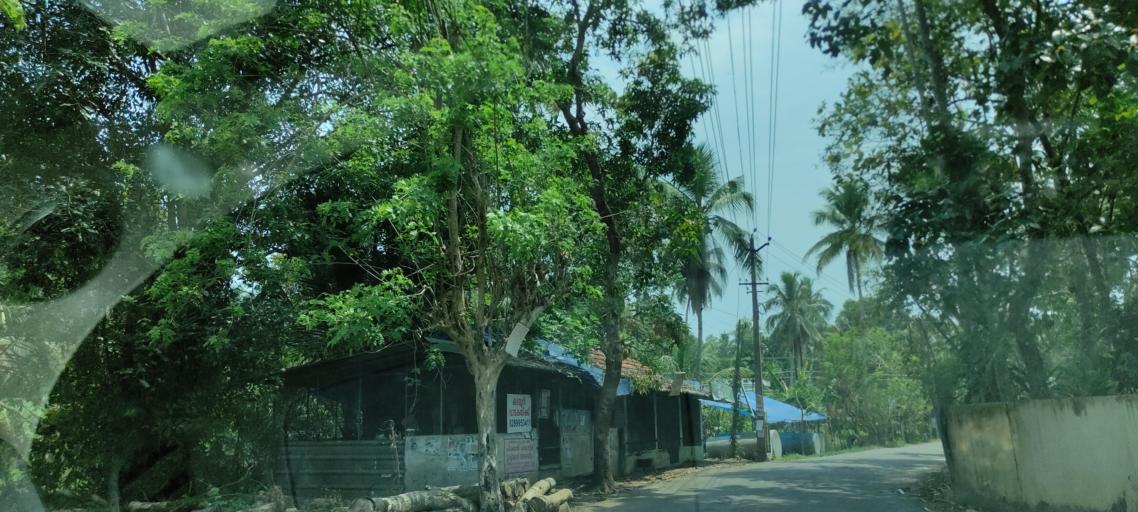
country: IN
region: Kerala
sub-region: Alappuzha
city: Vayalar
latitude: 9.7237
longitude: 76.3284
